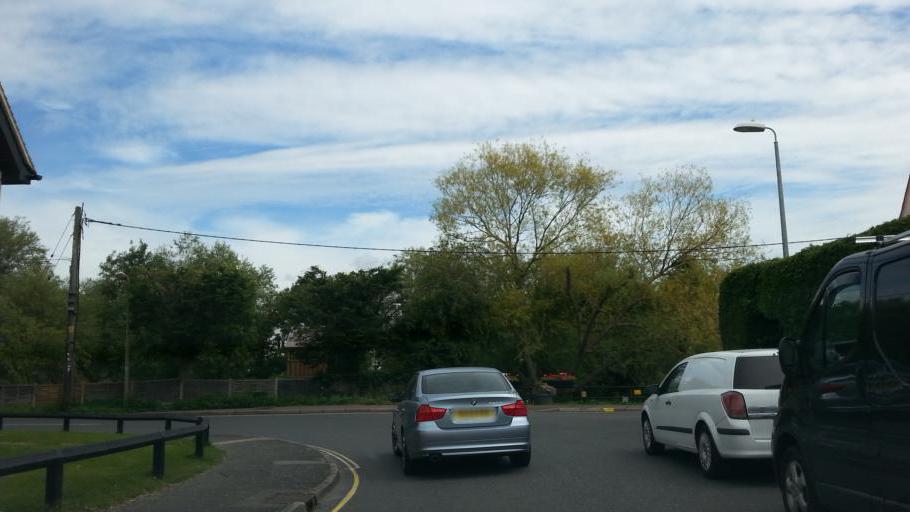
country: GB
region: England
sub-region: Essex
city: Kelvedon
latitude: 51.8395
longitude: 0.7065
